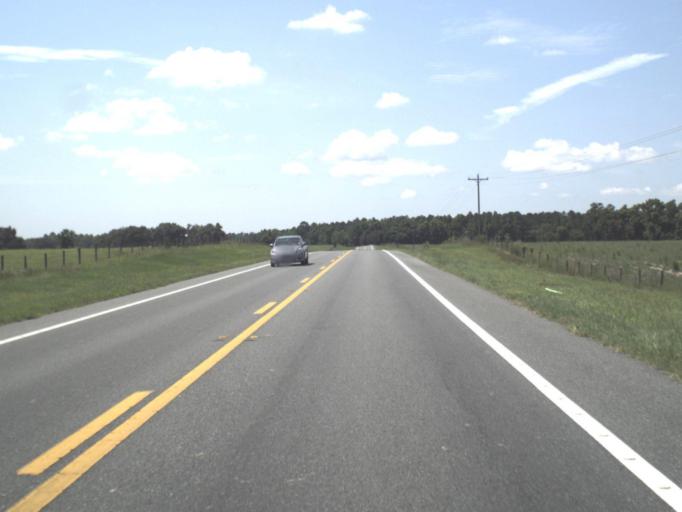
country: US
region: Florida
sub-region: Levy County
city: Williston
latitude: 29.4700
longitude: -82.4149
